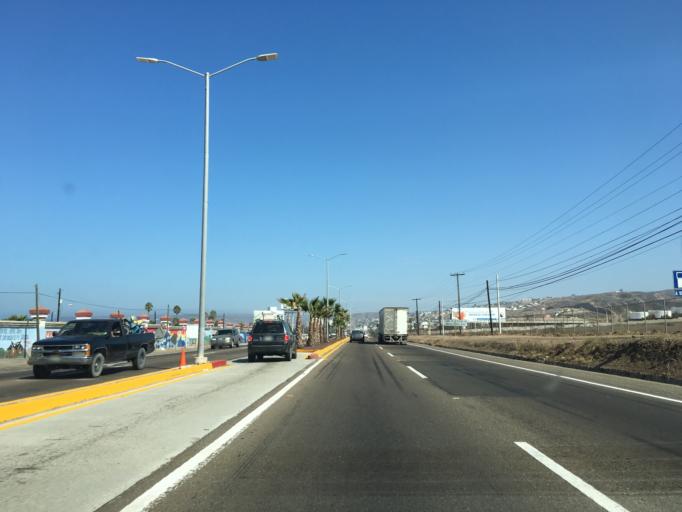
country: MX
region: Baja California
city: El Sauzal
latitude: 31.8777
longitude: -116.6814
